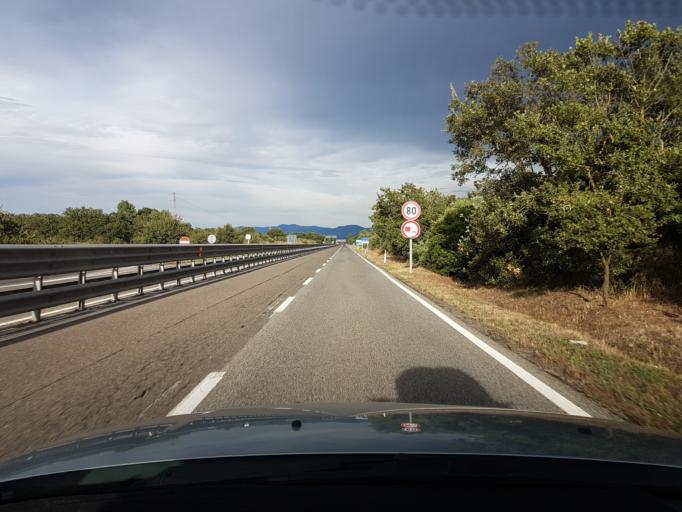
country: IT
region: Sardinia
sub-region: Provincia di Oristano
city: Abbasanta
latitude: 40.1147
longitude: 8.8191
